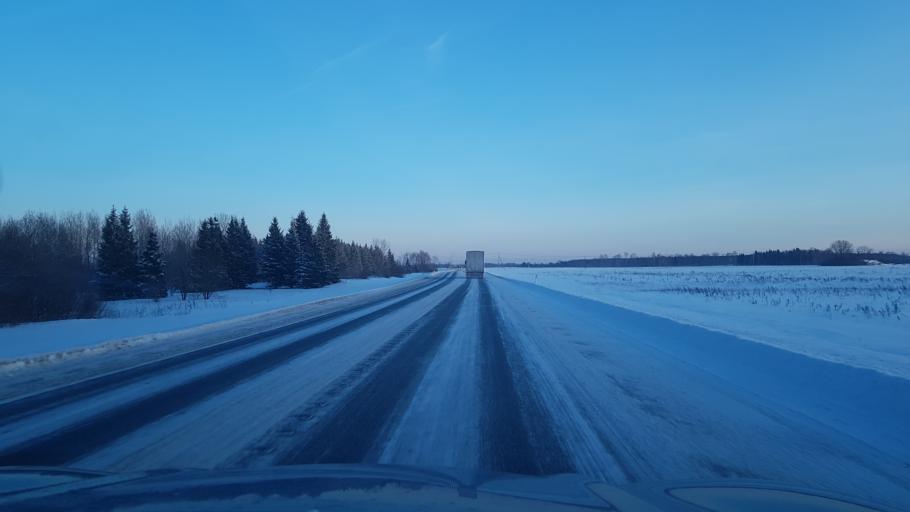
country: EE
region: Ida-Virumaa
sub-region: Narva-Joesuu linn
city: Narva-Joesuu
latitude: 59.3932
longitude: 28.0855
